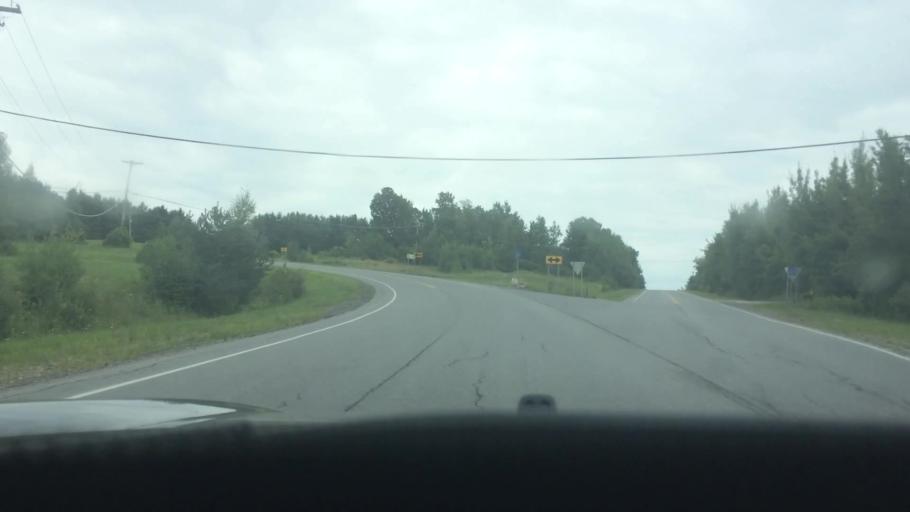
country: US
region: New York
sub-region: St. Lawrence County
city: Canton
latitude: 44.5430
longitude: -75.1003
